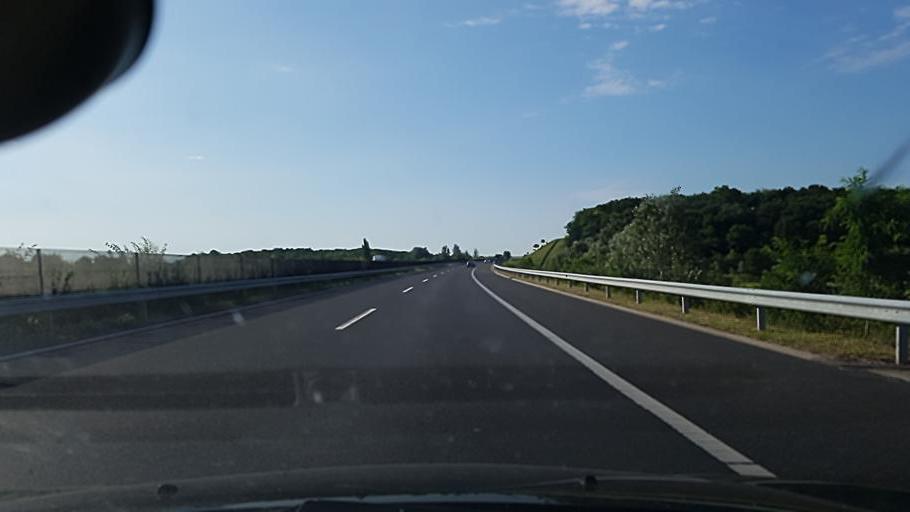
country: HU
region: Fejer
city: Adony
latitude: 47.0791
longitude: 18.8745
